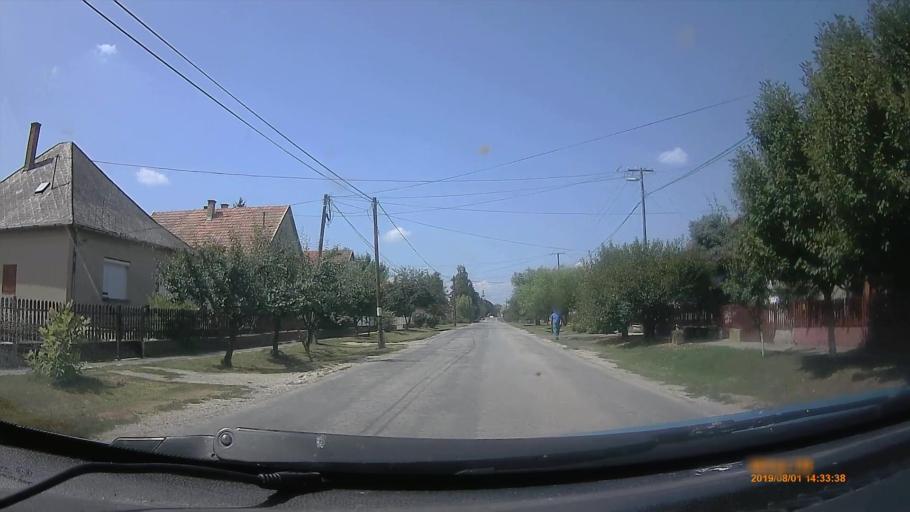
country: HR
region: Osjecko-Baranjska
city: Viljevo
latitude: 45.8209
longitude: 18.1043
